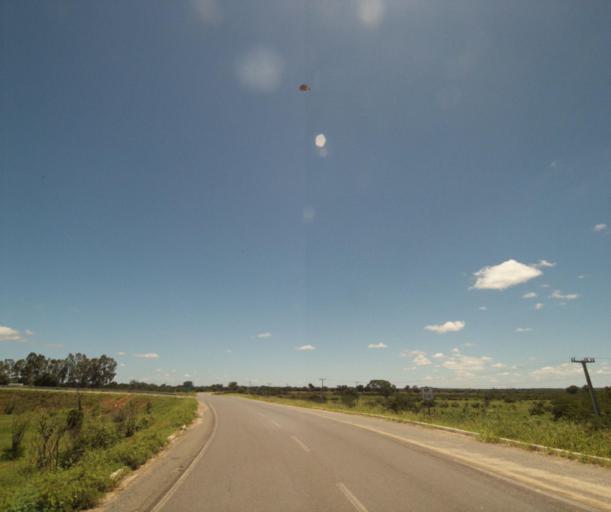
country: BR
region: Bahia
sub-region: Carinhanha
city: Carinhanha
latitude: -14.3289
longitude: -43.7642
